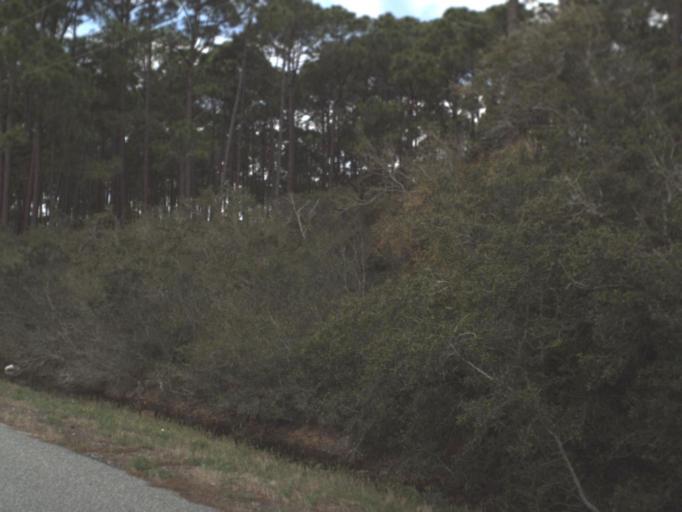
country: US
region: Florida
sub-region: Franklin County
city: Eastpoint
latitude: 29.7685
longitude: -84.8025
